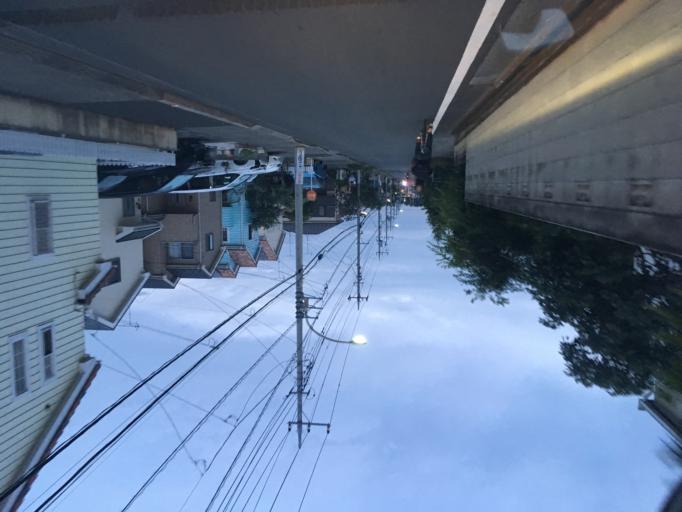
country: JP
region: Tokyo
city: Kokubunji
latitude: 35.7172
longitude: 139.4561
